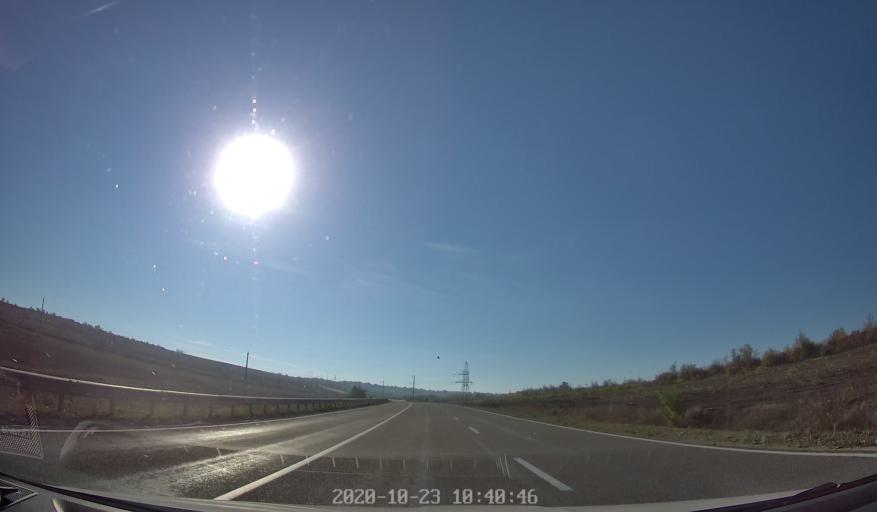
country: MD
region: Causeni
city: Causeni
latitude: 46.6397
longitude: 29.4586
